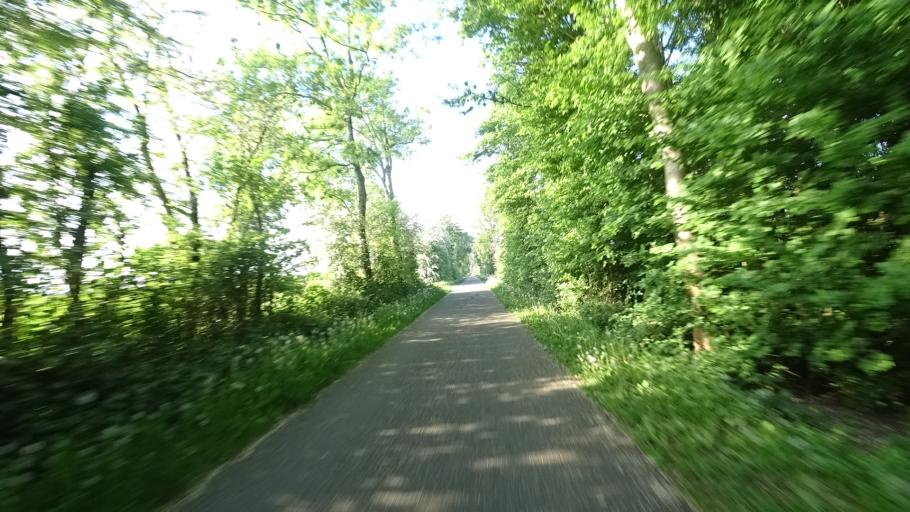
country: BE
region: Wallonia
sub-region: Province de Namur
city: Eghezee
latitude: 50.5324
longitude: 4.9008
